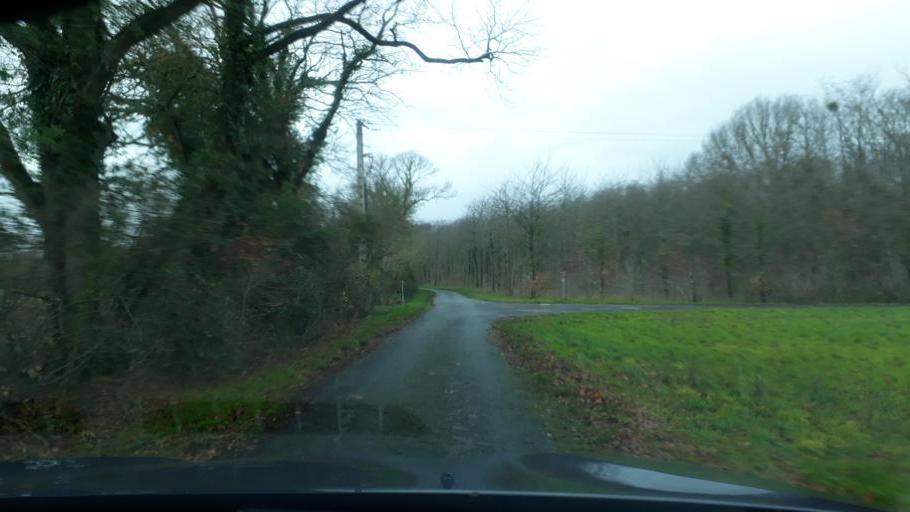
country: FR
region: Centre
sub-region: Departement du Loiret
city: Saint-Hilaire-Saint-Mesmin
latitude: 47.8463
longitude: 1.8388
